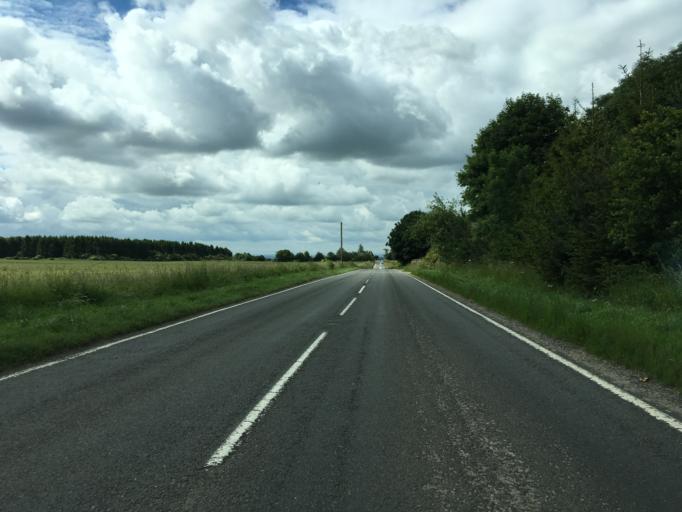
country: GB
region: England
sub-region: Oxfordshire
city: Shipton under Wychwood
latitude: 51.8335
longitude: -1.6080
